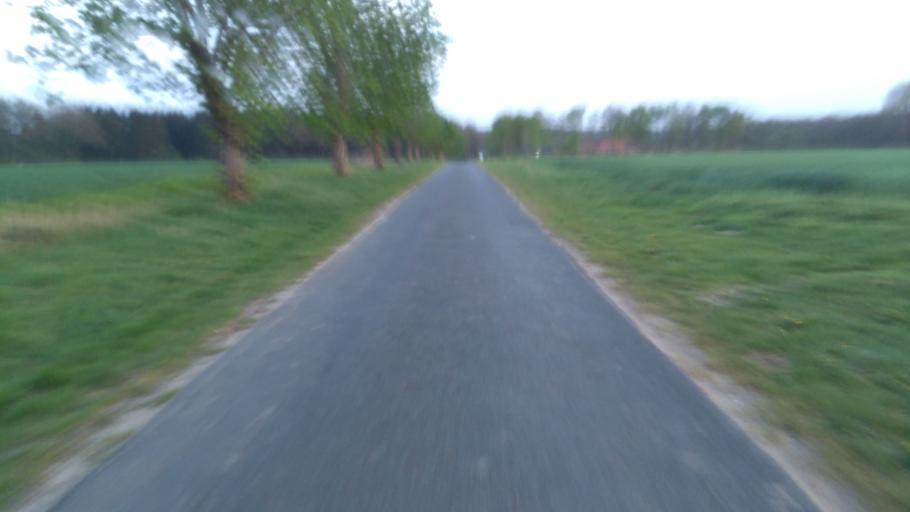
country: DE
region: Lower Saxony
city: Bargstedt
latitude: 53.4620
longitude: 9.4698
